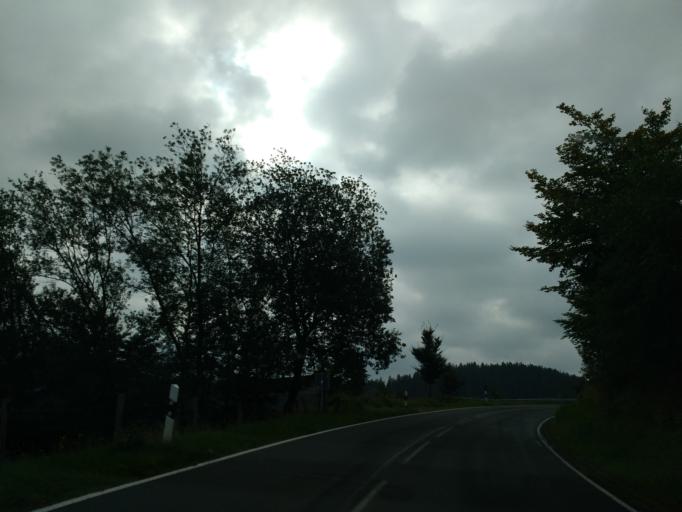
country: DE
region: North Rhine-Westphalia
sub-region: Regierungsbezirk Arnsberg
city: Bestwig
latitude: 51.3231
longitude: 8.4369
